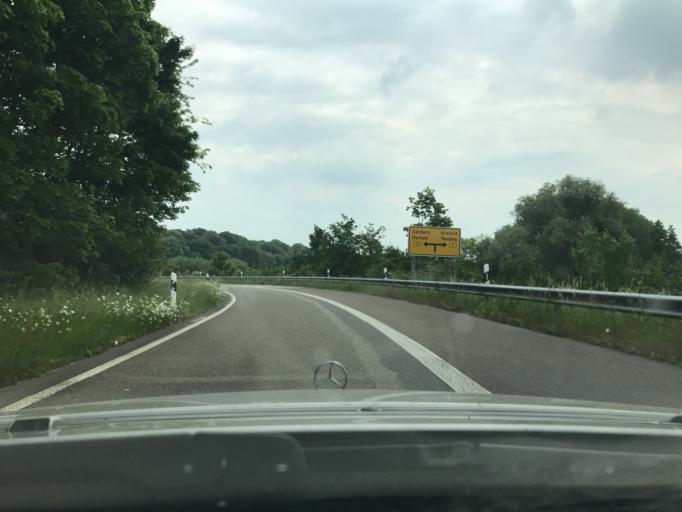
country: DE
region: North Rhine-Westphalia
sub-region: Regierungsbezirk Dusseldorf
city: Rheurdt
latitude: 51.4120
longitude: 6.4768
